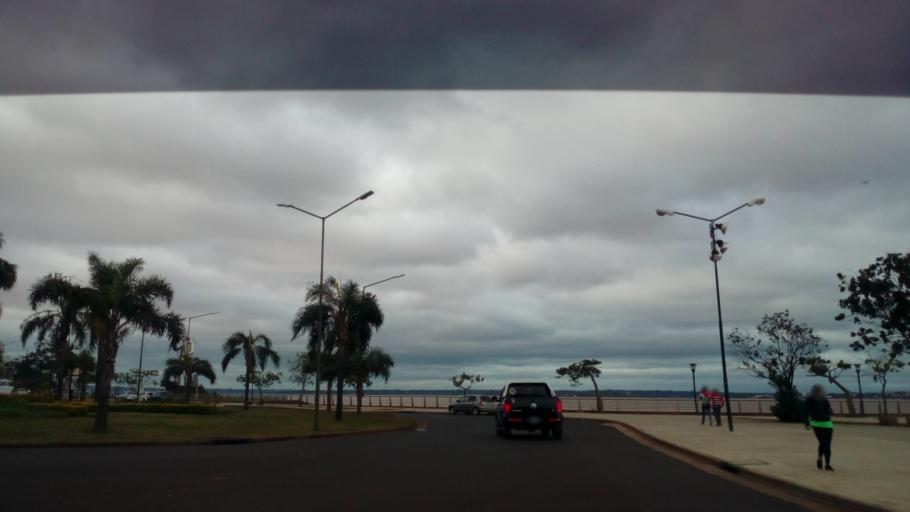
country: AR
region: Misiones
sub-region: Departamento de Capital
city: Posadas
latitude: -27.3619
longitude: -55.8866
